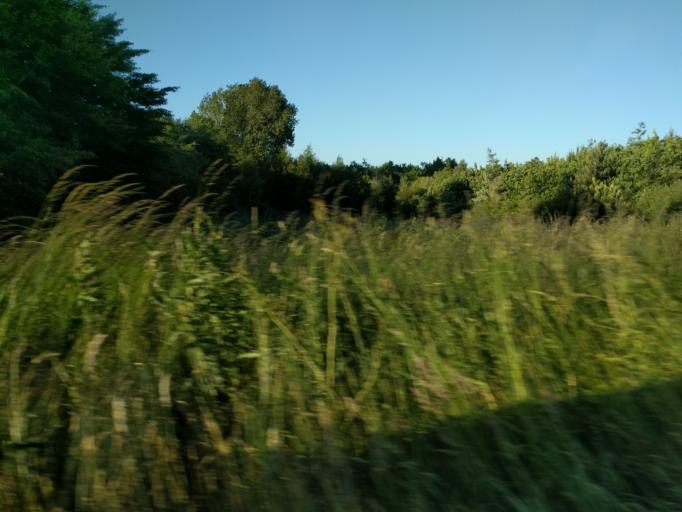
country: DK
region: South Denmark
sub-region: Kerteminde Kommune
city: Kerteminde
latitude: 55.5645
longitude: 10.6475
